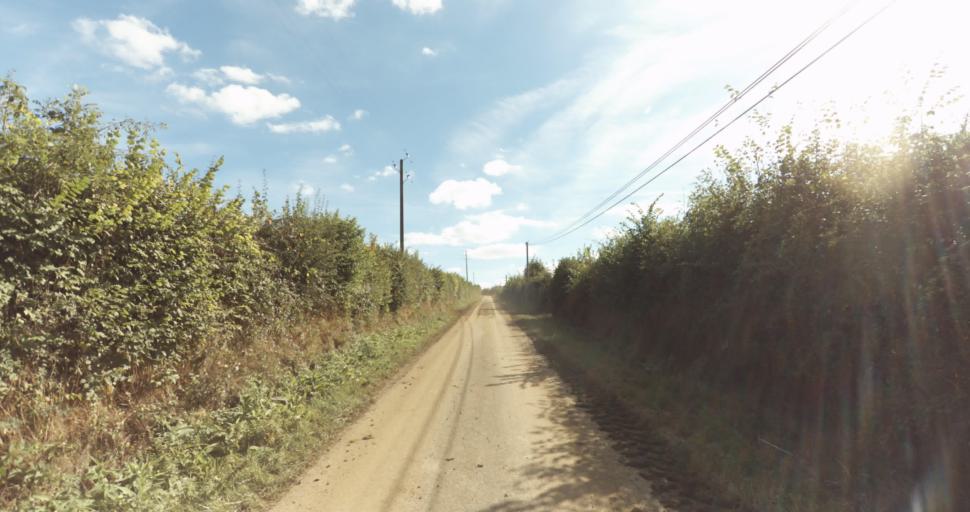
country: FR
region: Lower Normandy
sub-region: Departement de l'Orne
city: Vimoutiers
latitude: 48.9348
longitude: 0.1303
